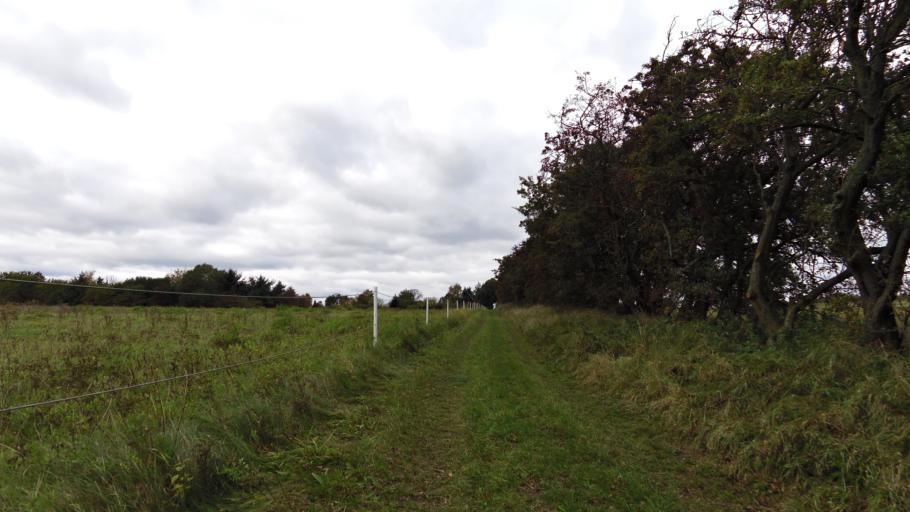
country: DK
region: Central Jutland
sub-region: Arhus Kommune
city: Kolt
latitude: 56.1430
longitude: 10.0596
